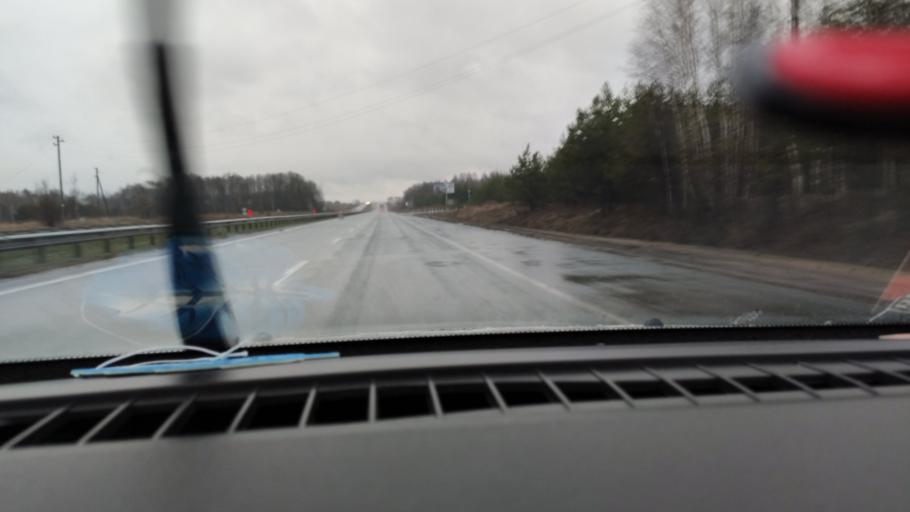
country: RU
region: Tatarstan
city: Yelabuga
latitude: 55.7950
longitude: 52.1538
